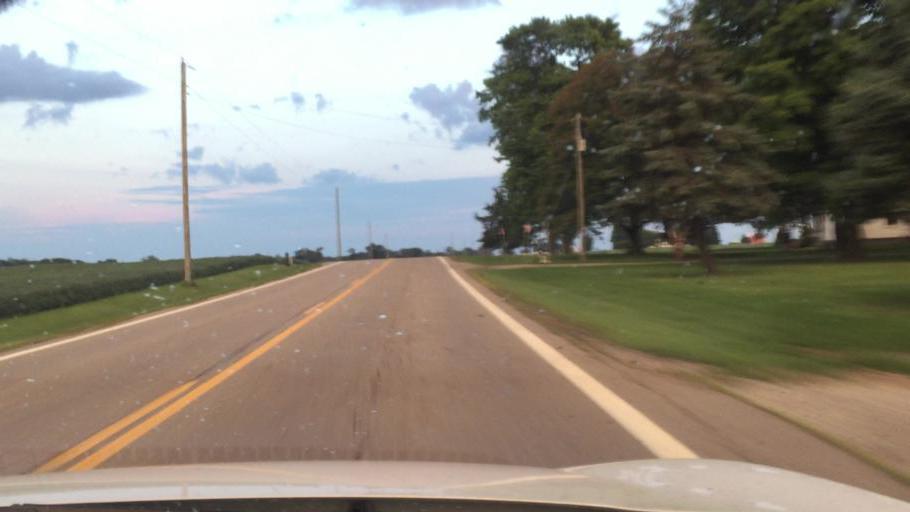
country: US
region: Ohio
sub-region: Madison County
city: Choctaw Lake
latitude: 40.0329
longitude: -83.4934
